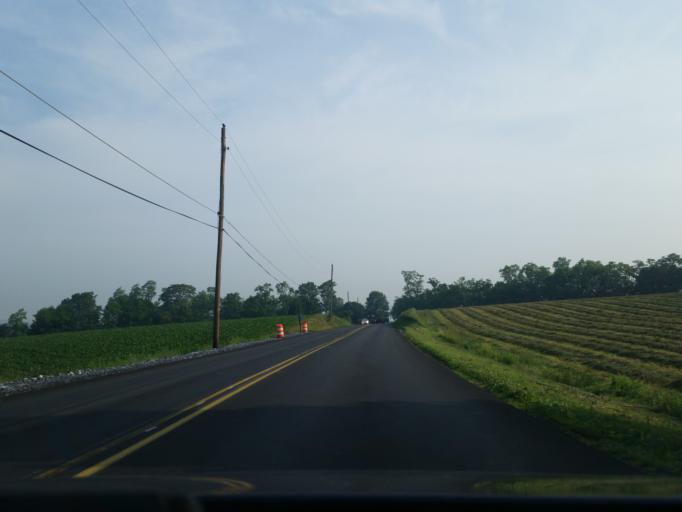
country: US
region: Pennsylvania
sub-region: Lebanon County
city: Annville
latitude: 40.3816
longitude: -76.5566
